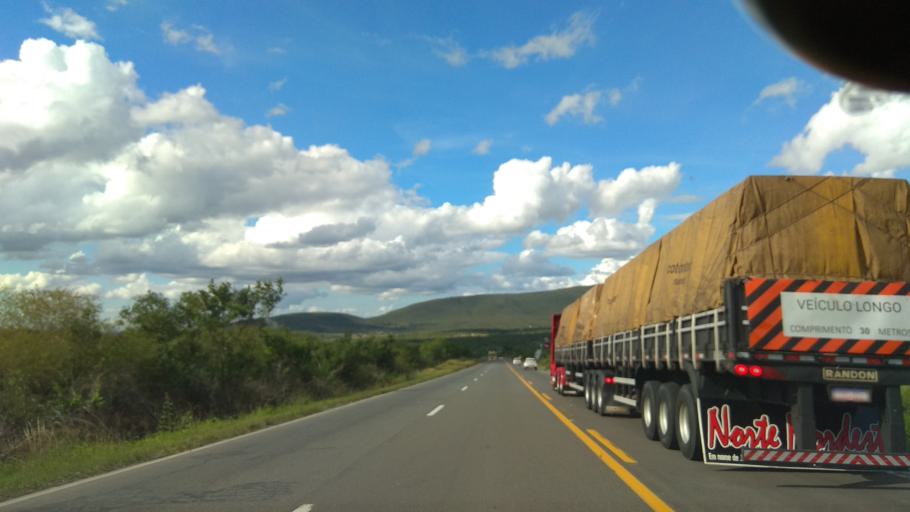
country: BR
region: Bahia
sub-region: Castro Alves
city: Castro Alves
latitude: -12.6526
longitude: -39.6126
